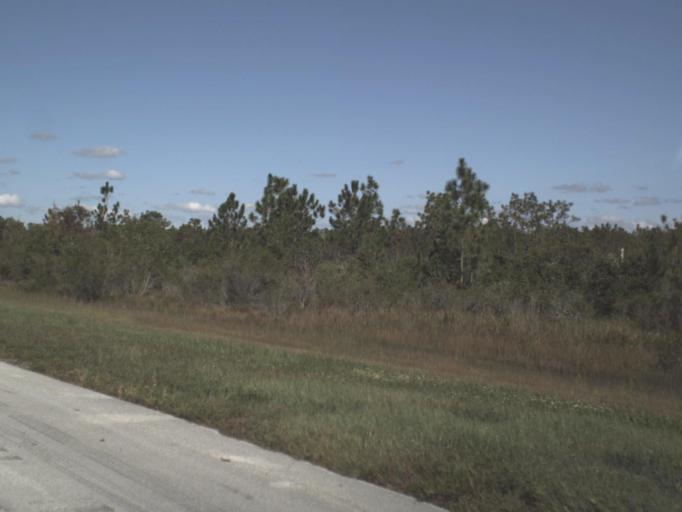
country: US
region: Florida
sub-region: Osceola County
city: Saint Cloud
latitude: 28.0018
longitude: -81.1399
